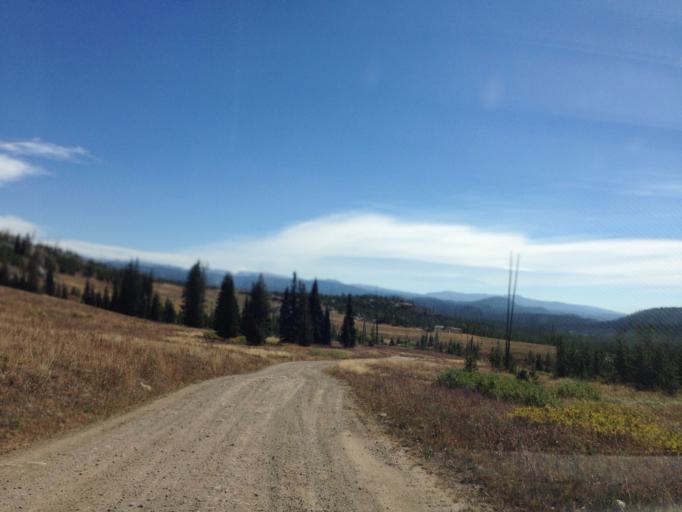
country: US
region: Montana
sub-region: Stillwater County
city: Absarokee
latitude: 45.0323
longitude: -109.9069
